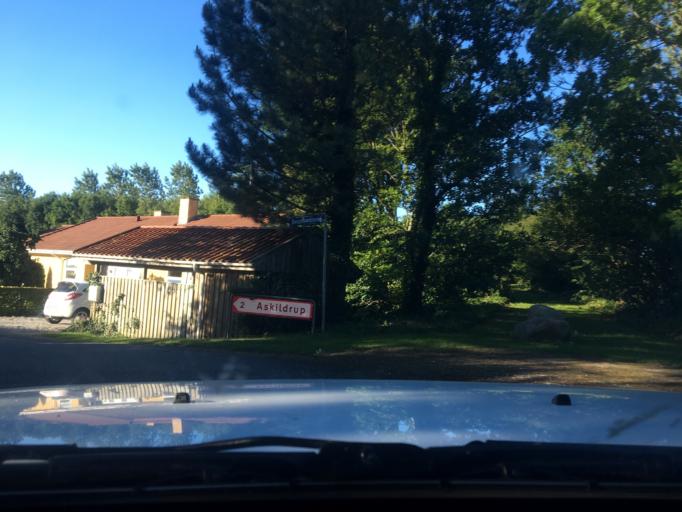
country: DK
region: Central Jutland
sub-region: Randers Kommune
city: Randers
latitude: 56.4088
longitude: 10.0530
